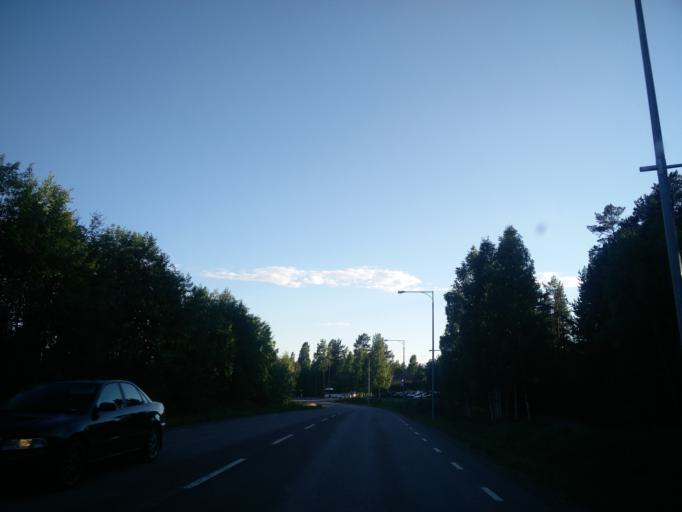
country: SE
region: Vaesternorrland
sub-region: Sundsvalls Kommun
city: Sundsvall
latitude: 62.4166
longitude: 17.2591
